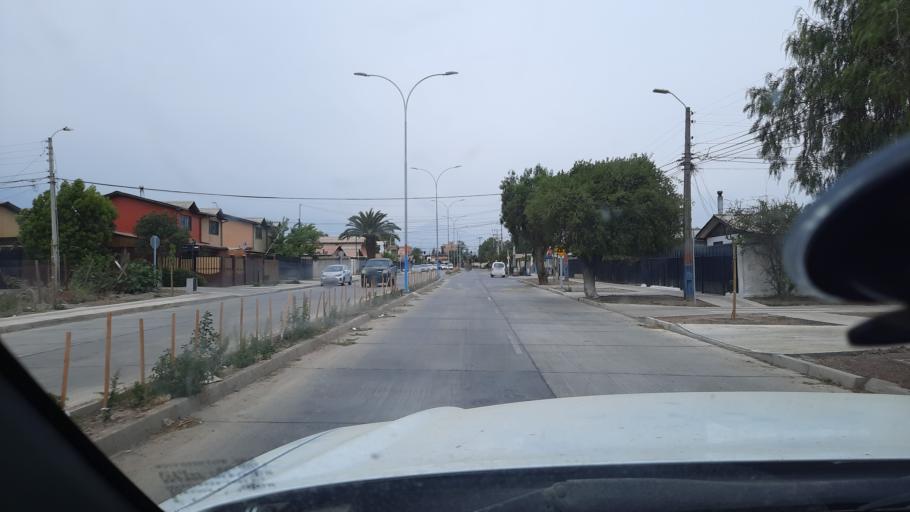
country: CL
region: Valparaiso
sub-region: Provincia de San Felipe
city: San Felipe
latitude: -32.7432
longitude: -70.7194
